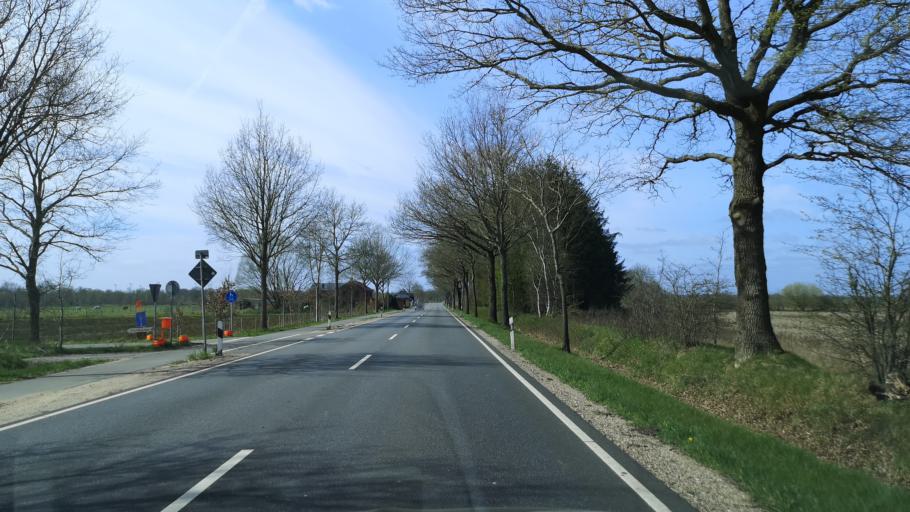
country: DE
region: Schleswig-Holstein
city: Prinzenmoor
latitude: 54.2223
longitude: 9.4732
